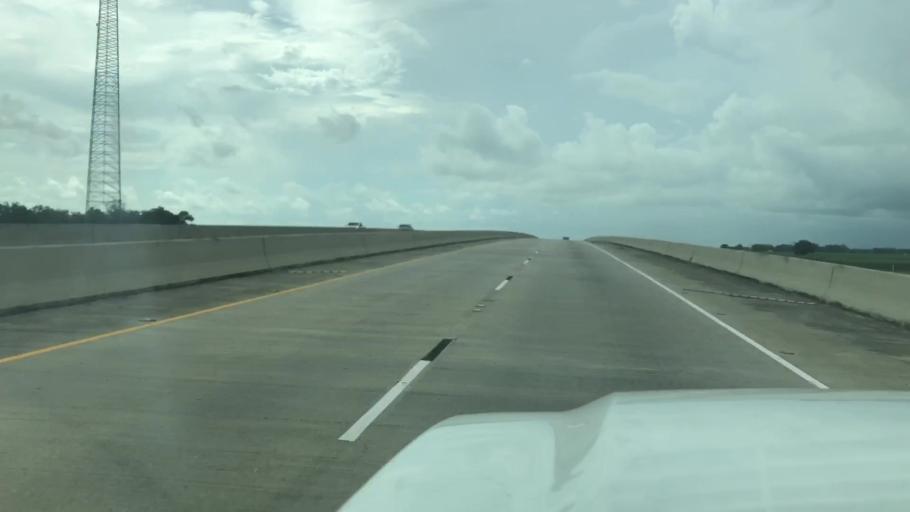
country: US
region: Louisiana
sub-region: Iberia Parish
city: Jeanerette
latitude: 29.9188
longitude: -91.7270
